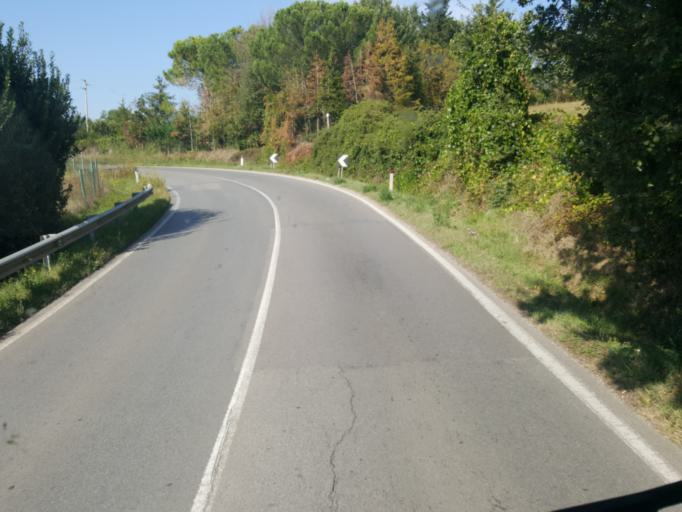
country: IT
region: Tuscany
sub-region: Provincia di Siena
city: Colle di Val d'Elsa
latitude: 43.4139
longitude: 11.1056
